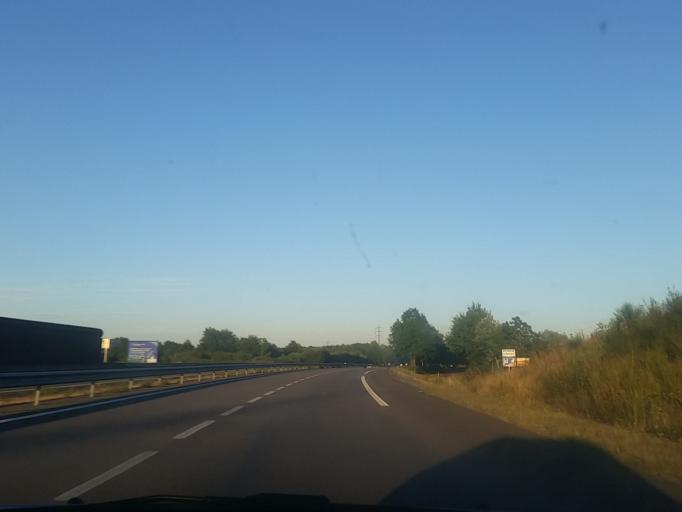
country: FR
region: Pays de la Loire
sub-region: Departement de la Loire-Atlantique
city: La Montagne
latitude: 47.1754
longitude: -1.6902
